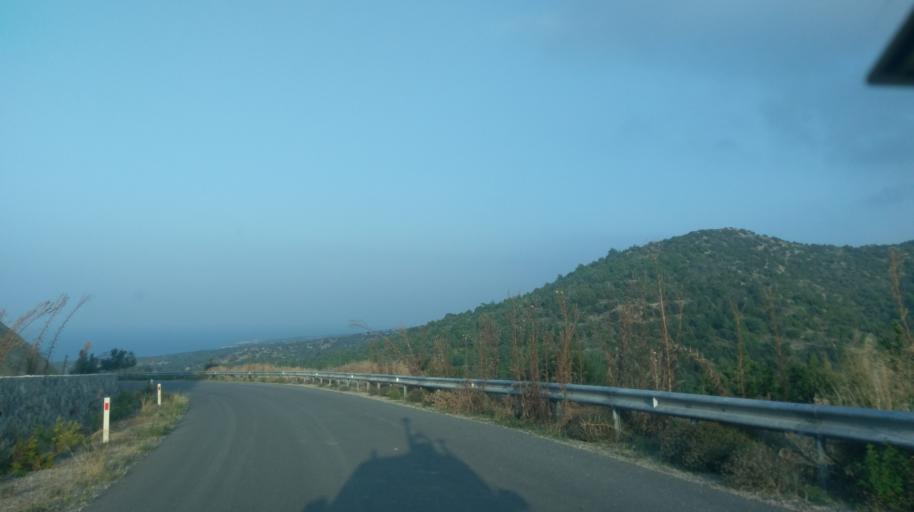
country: CY
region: Ammochostos
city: Trikomo
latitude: 35.4006
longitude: 33.8585
